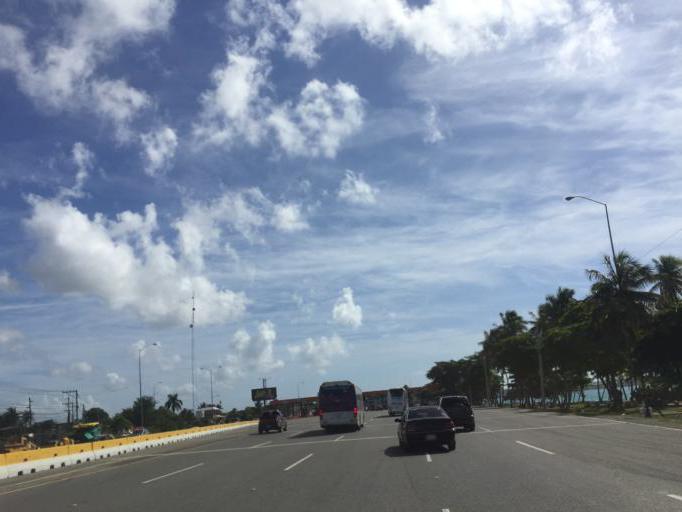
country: DO
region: Santo Domingo
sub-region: Santo Domingo
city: Boca Chica
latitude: 18.4535
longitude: -69.6933
